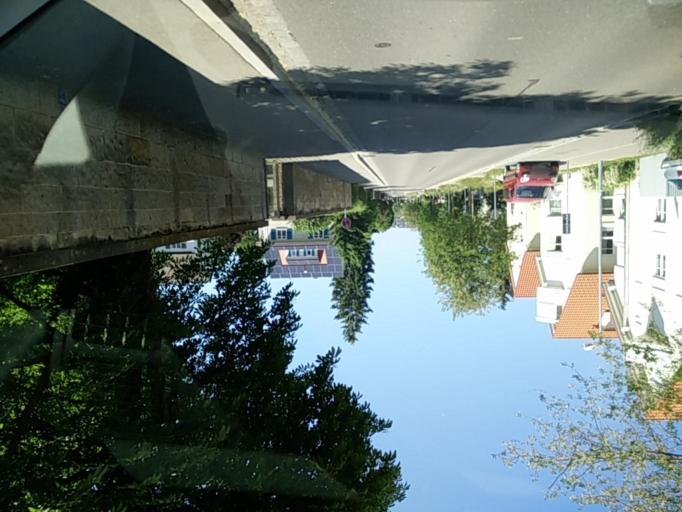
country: DE
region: Baden-Wuerttemberg
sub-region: Tuebingen Region
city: Tuebingen
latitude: 48.5081
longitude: 9.0515
